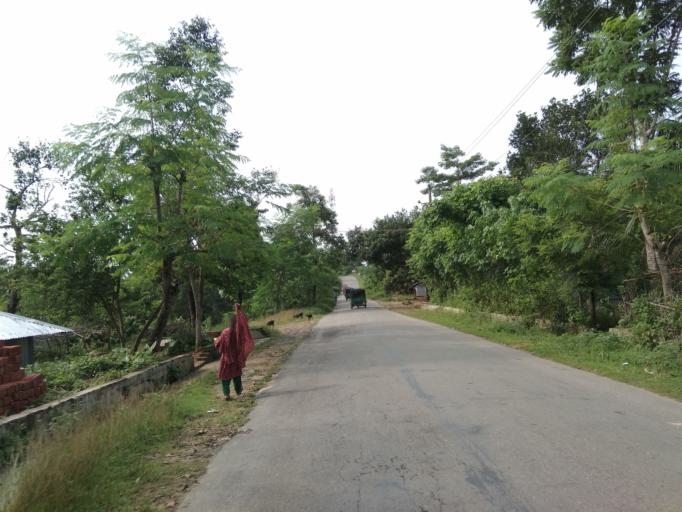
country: BD
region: Chittagong
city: Khagrachhari
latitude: 22.9985
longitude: 92.0112
